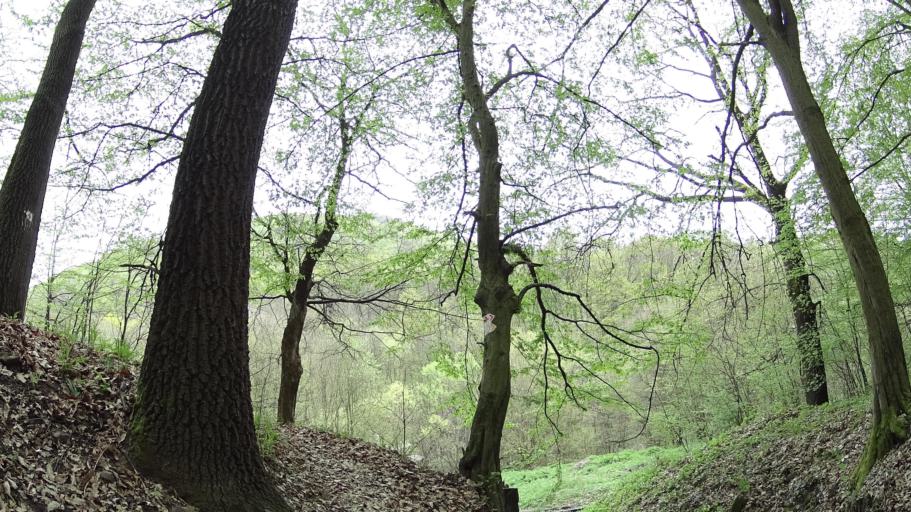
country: HU
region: Pest
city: Kismaros
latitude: 47.8824
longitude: 19.0293
